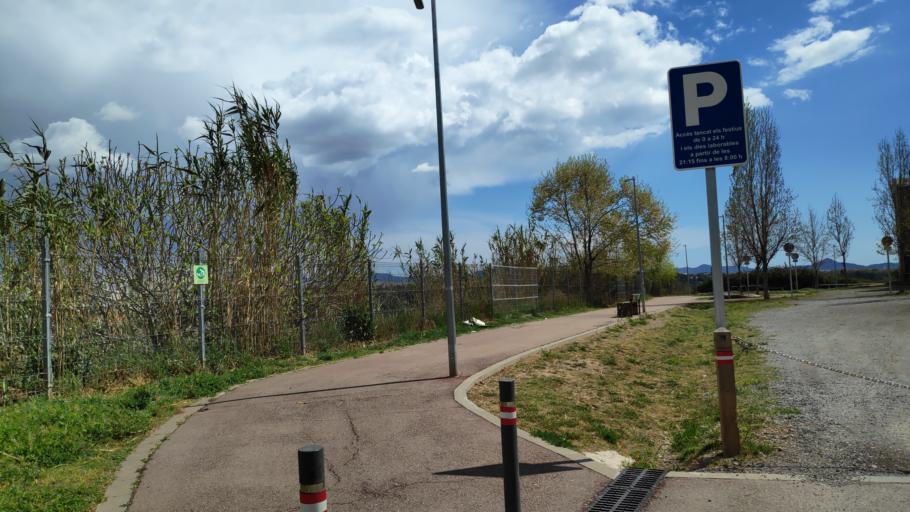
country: ES
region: Catalonia
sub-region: Provincia de Barcelona
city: Sabadell
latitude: 41.5472
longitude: 2.1195
